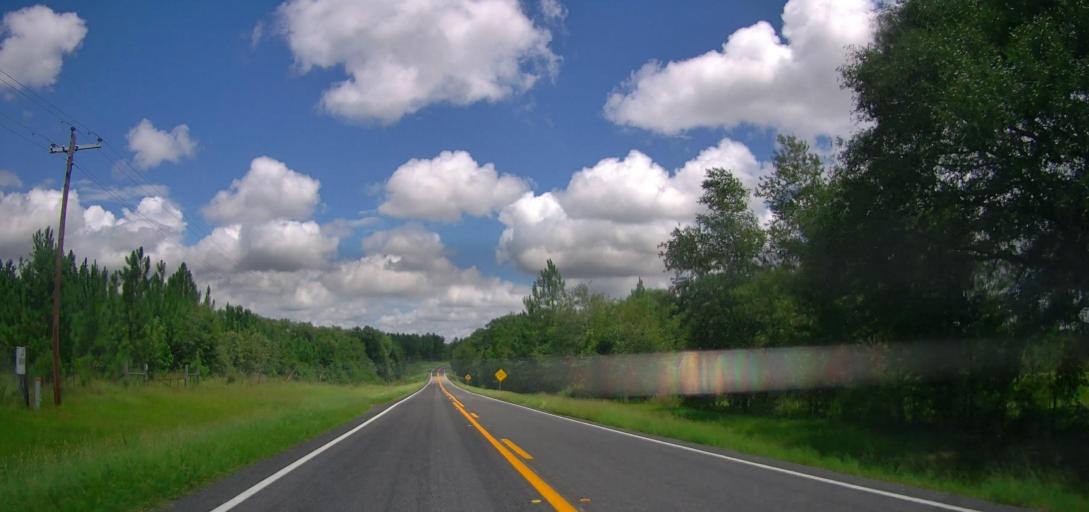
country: US
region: Georgia
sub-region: Turner County
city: Ashburn
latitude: 31.7823
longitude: -83.6047
